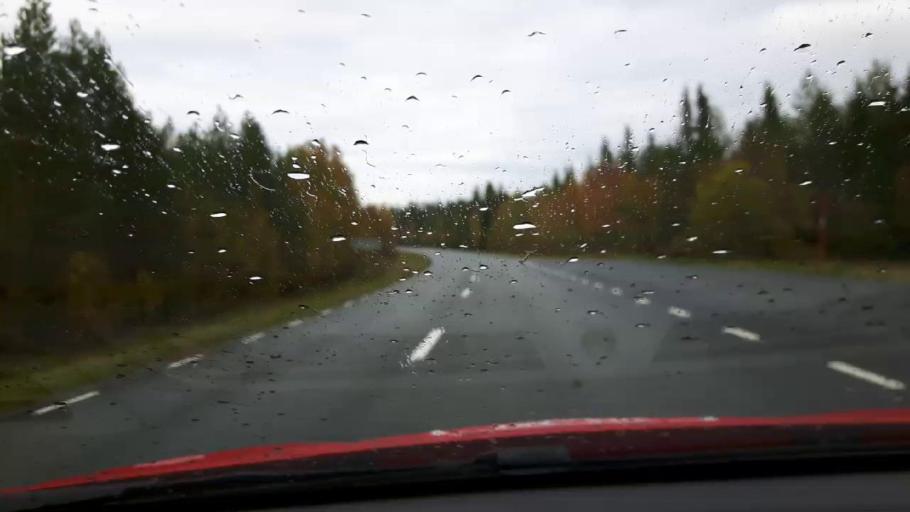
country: SE
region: Jaemtland
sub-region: Krokoms Kommun
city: Krokom
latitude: 63.0929
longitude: 14.3020
